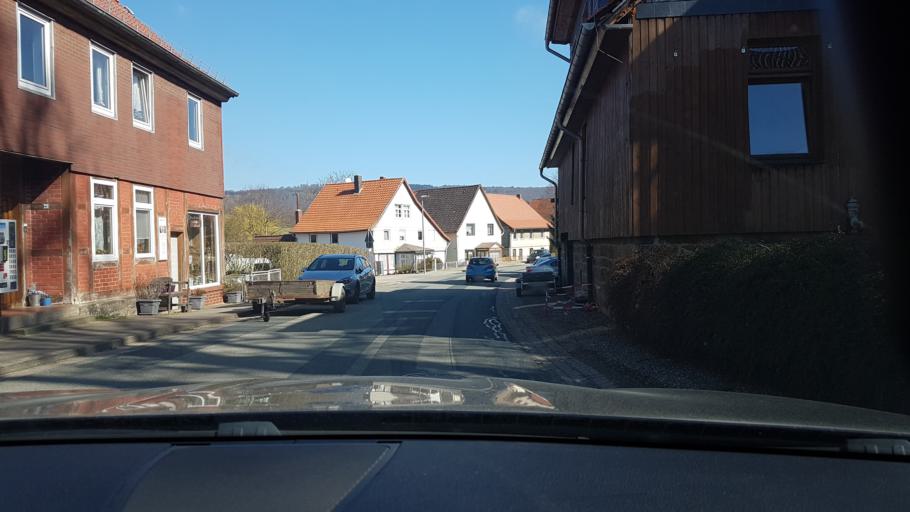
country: DE
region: Lower Saxony
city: Coppenbrugge
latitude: 52.1327
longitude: 9.5630
